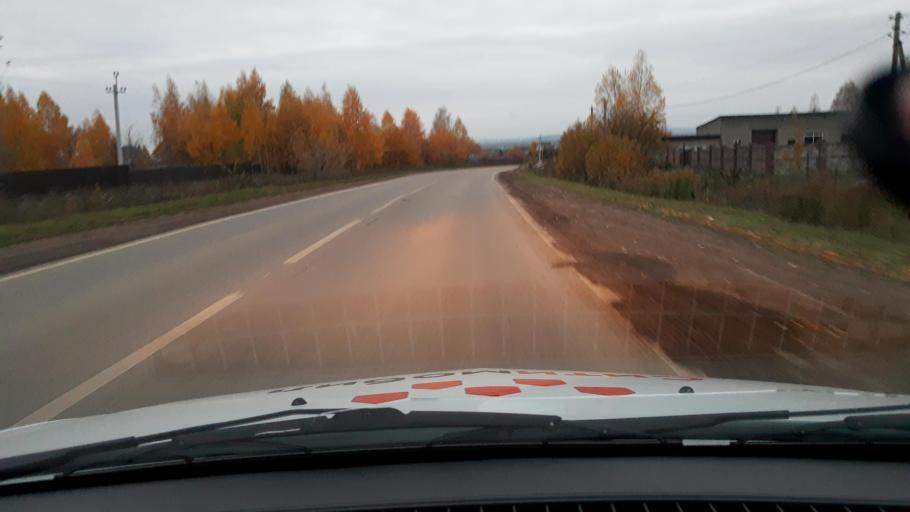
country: RU
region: Bashkortostan
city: Kabakovo
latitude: 54.7076
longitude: 56.1685
